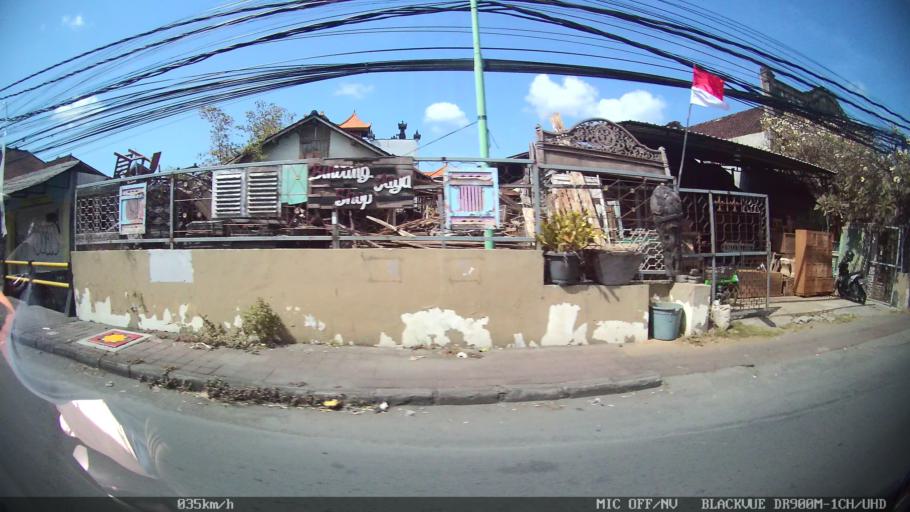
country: ID
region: Bali
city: Denpasar
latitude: -8.6722
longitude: 115.1712
